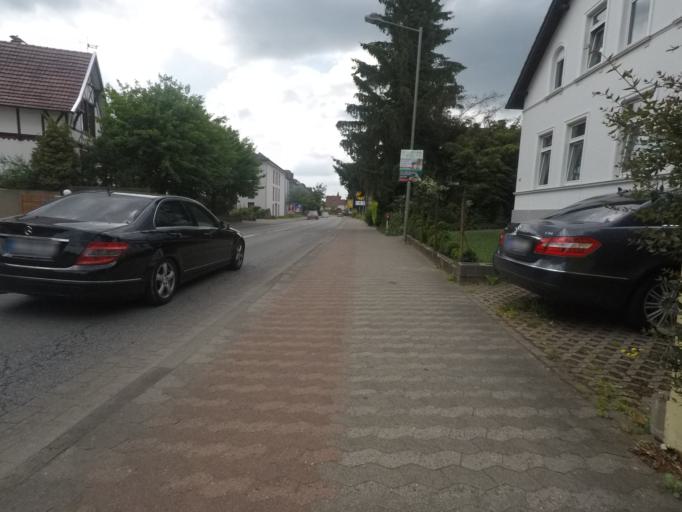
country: DE
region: North Rhine-Westphalia
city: Buende
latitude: 52.1936
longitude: 8.5890
